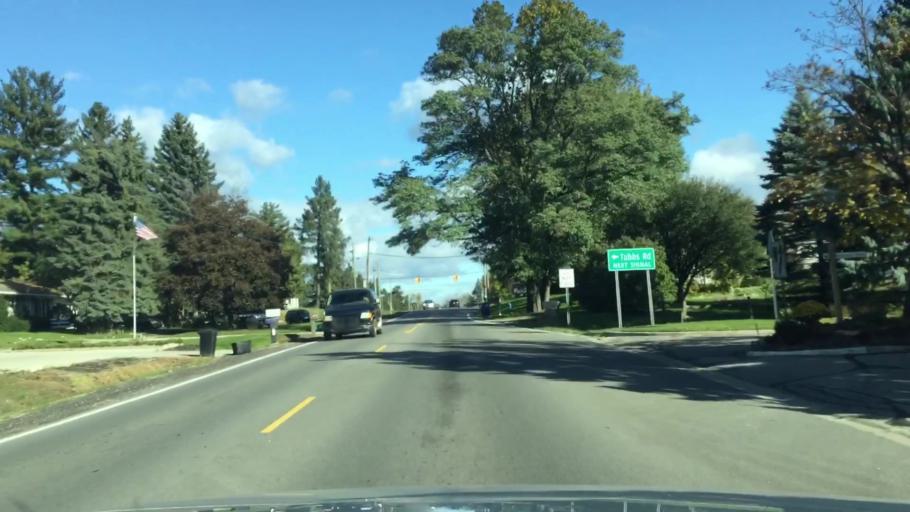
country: US
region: Michigan
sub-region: Oakland County
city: Waterford
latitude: 42.6662
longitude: -83.3865
